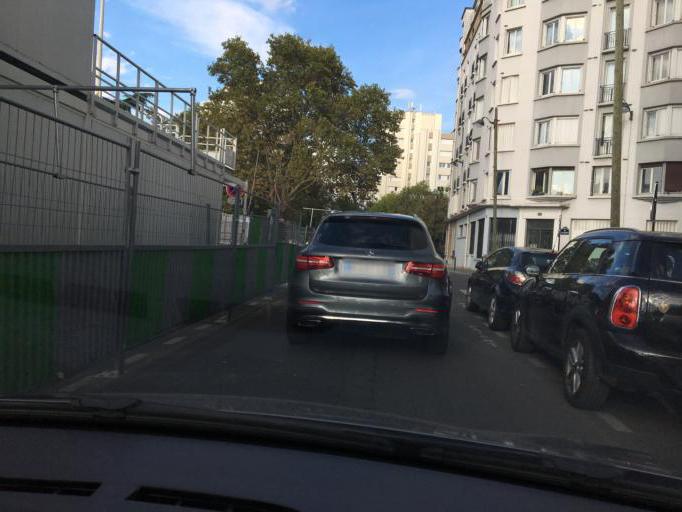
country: FR
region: Ile-de-France
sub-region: Departement des Hauts-de-Seine
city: Clichy
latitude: 48.8906
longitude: 2.3015
